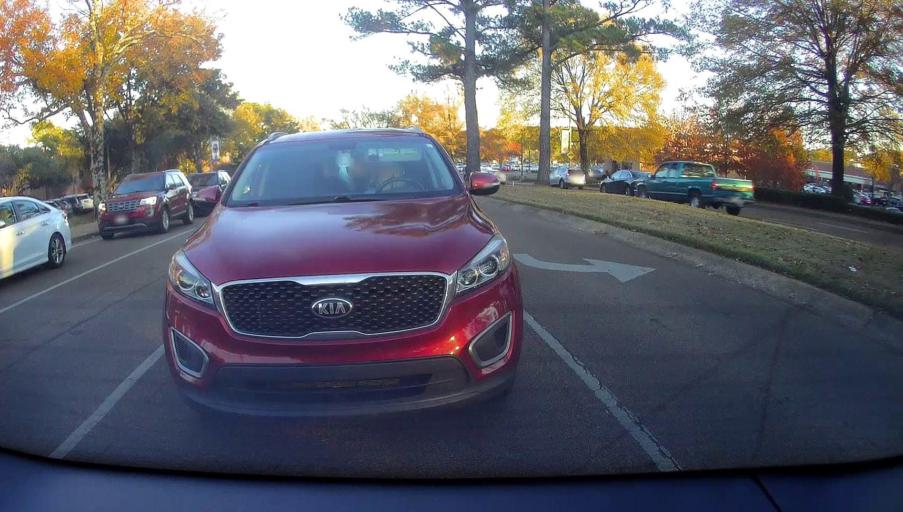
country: US
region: Tennessee
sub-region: Shelby County
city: Germantown
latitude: 35.0955
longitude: -89.8070
